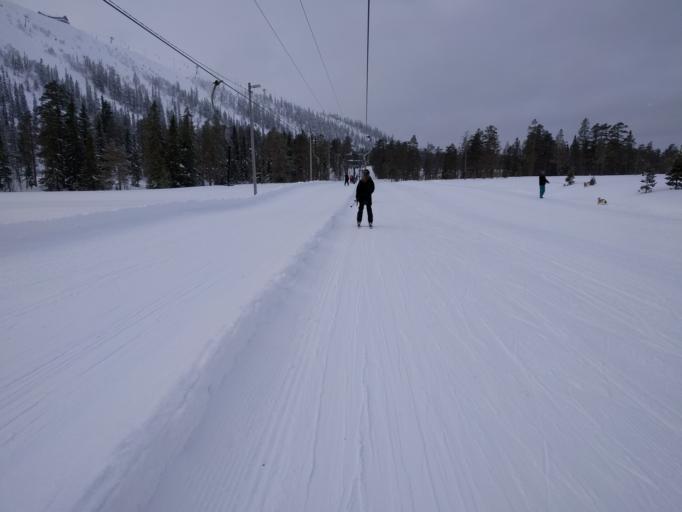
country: NO
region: Hedmark
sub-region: Trysil
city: Innbygda
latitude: 61.1736
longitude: 12.9886
